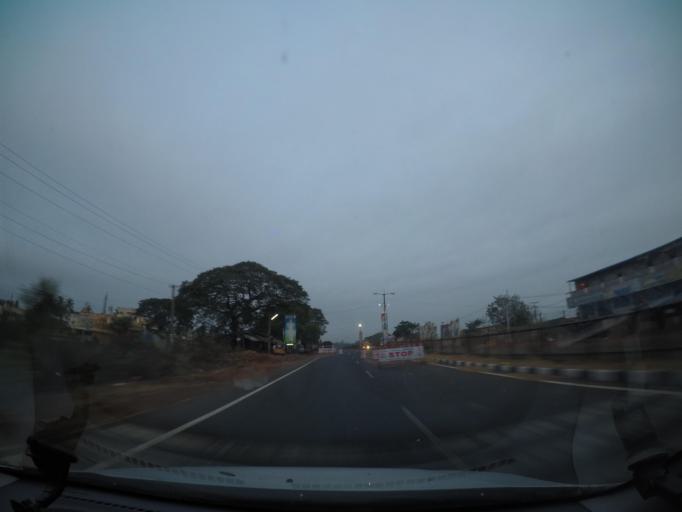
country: IN
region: Andhra Pradesh
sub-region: West Godavari
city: Tadepallegudem
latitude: 16.8093
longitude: 81.3244
